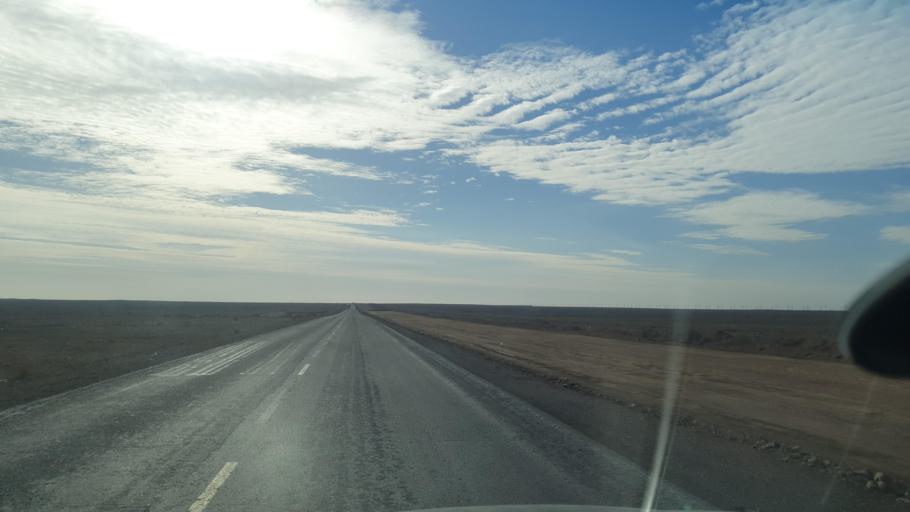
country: KZ
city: Priozersk
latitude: 45.9627
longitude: 73.5442
